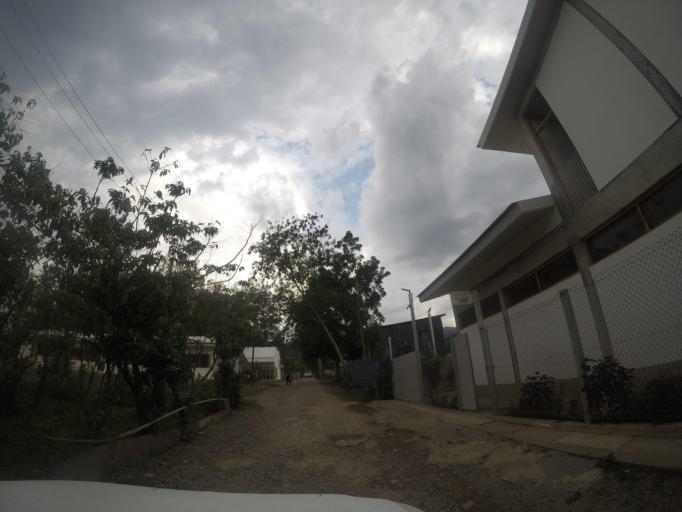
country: TL
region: Ermera
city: Gleno
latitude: -8.7264
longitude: 125.4446
